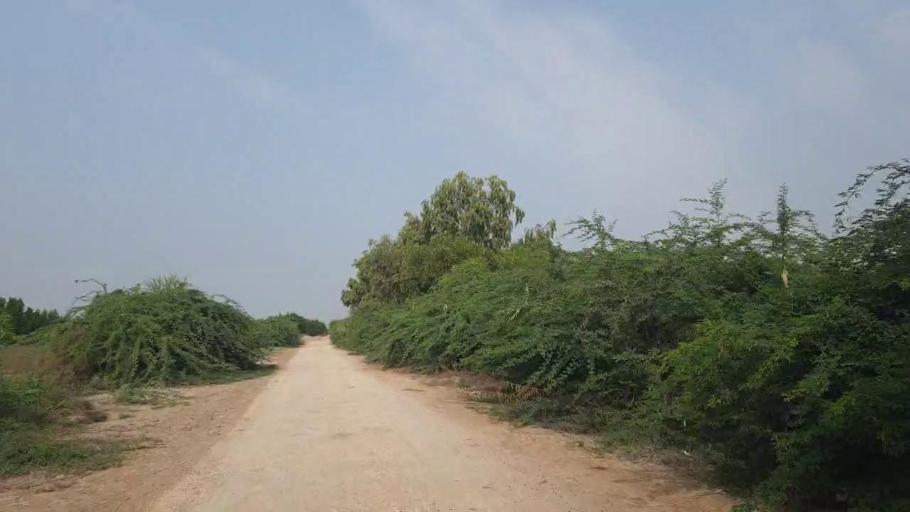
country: PK
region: Sindh
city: Badin
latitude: 24.6016
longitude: 68.7413
